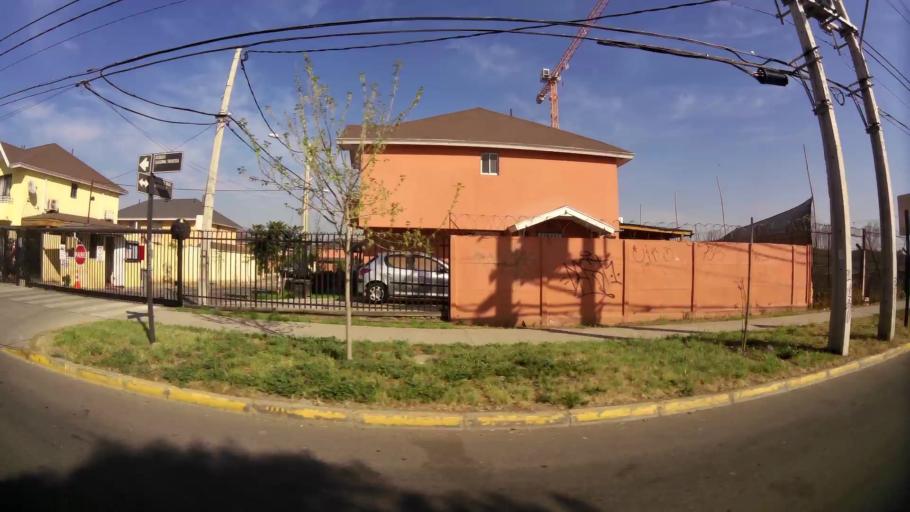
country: CL
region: Santiago Metropolitan
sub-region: Provincia de Santiago
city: Lo Prado
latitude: -33.4516
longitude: -70.7566
